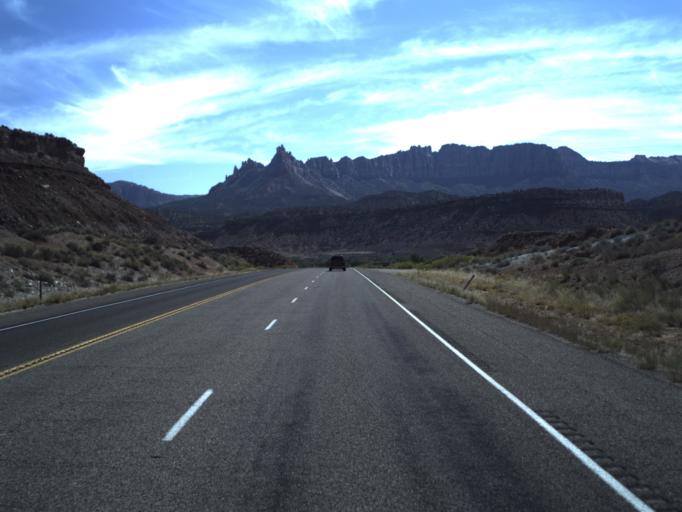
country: US
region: Utah
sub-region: Washington County
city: Hildale
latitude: 37.1691
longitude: -113.0662
